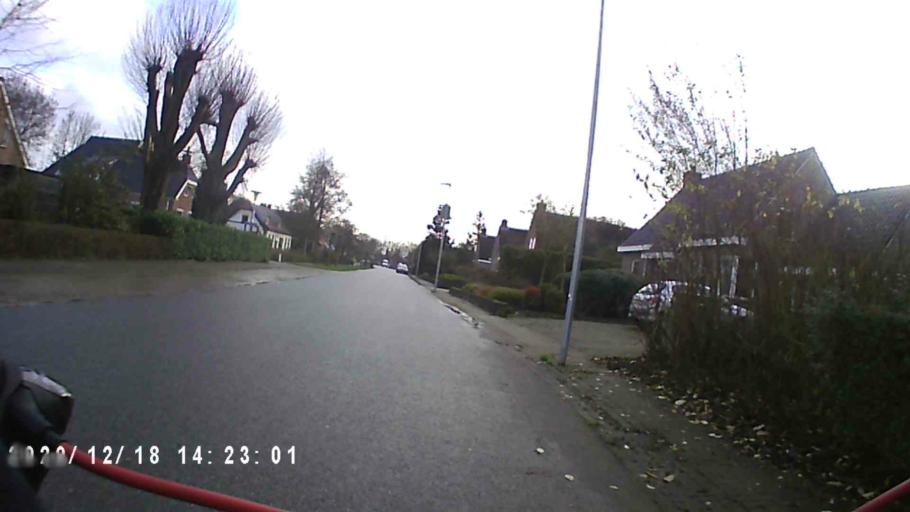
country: NL
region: Groningen
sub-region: Gemeente Groningen
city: Oosterpark
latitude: 53.2470
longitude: 6.6487
